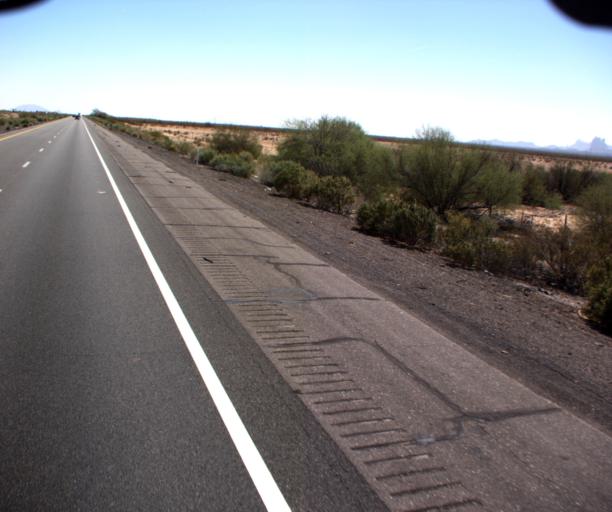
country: US
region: Arizona
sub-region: La Paz County
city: Salome
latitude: 33.5843
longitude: -113.4566
